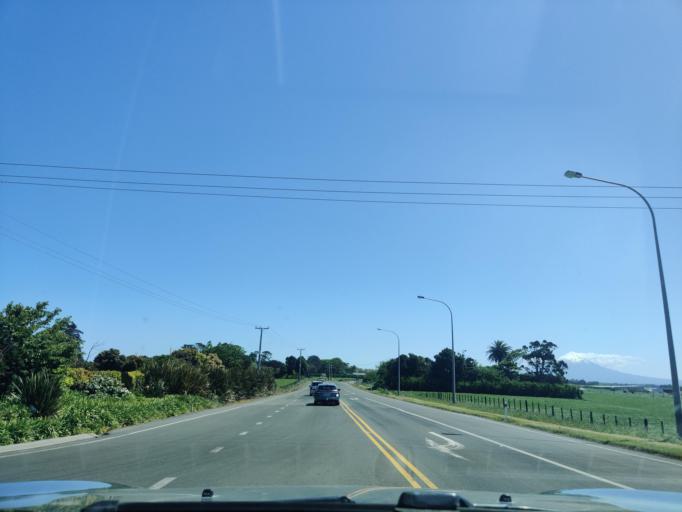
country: NZ
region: Taranaki
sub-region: South Taranaki District
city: Hawera
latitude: -39.6027
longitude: 174.3090
